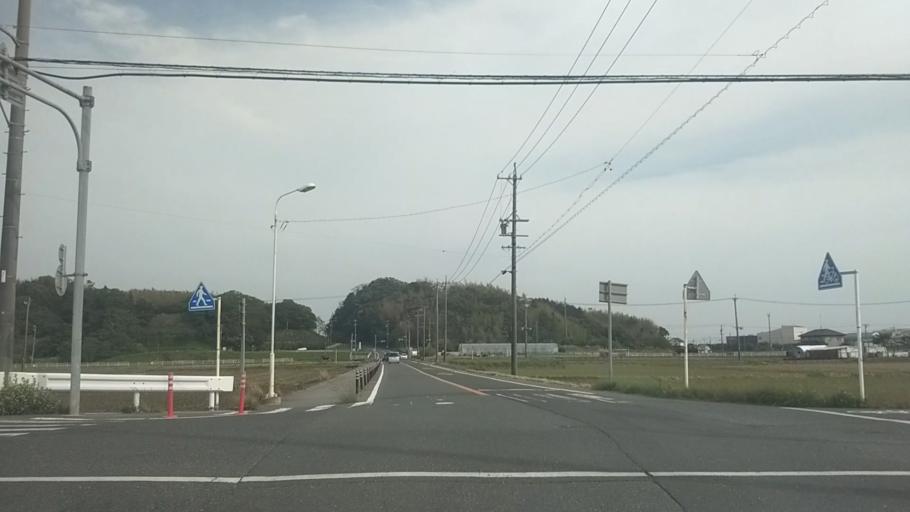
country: JP
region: Shizuoka
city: Kosai-shi
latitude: 34.7094
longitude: 137.6319
